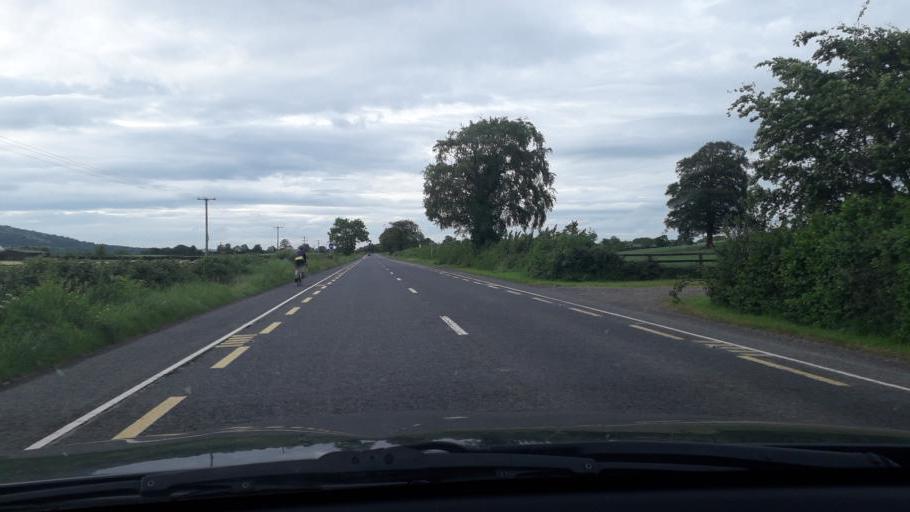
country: IE
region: Leinster
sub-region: County Carlow
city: Carlow
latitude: 52.7974
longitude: -6.9490
